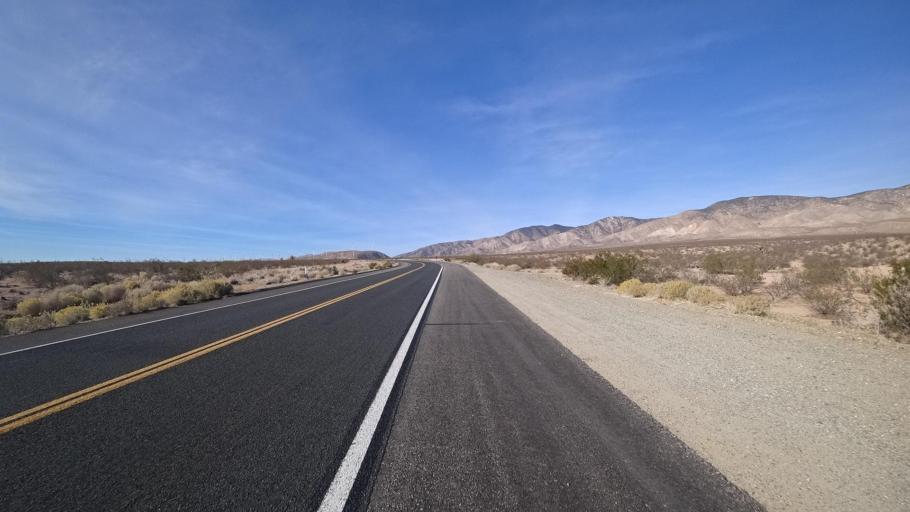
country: US
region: California
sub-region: Kern County
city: Mojave
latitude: 35.1258
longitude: -118.1726
